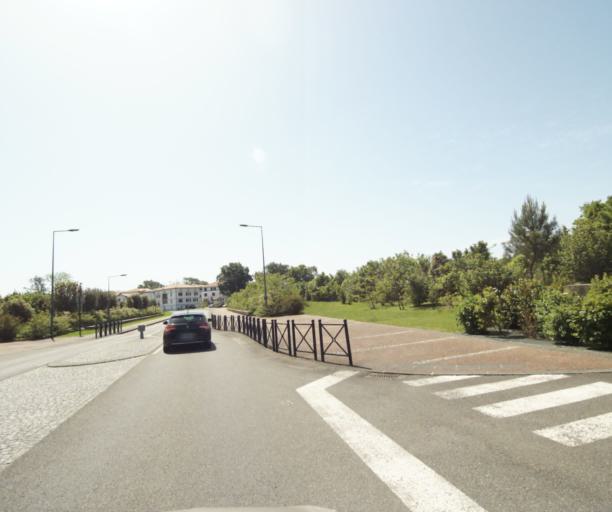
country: FR
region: Aquitaine
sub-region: Departement des Pyrenees-Atlantiques
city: Bayonne
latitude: 43.4753
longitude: -1.4553
